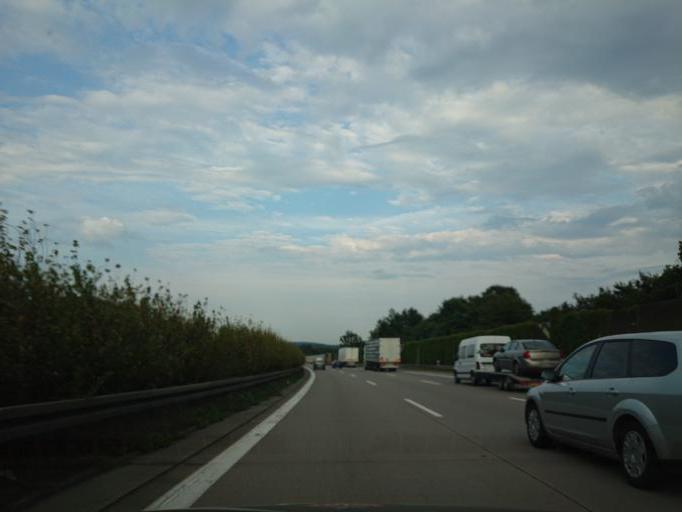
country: DE
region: Brandenburg
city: Wildau
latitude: 52.3102
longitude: 13.6271
